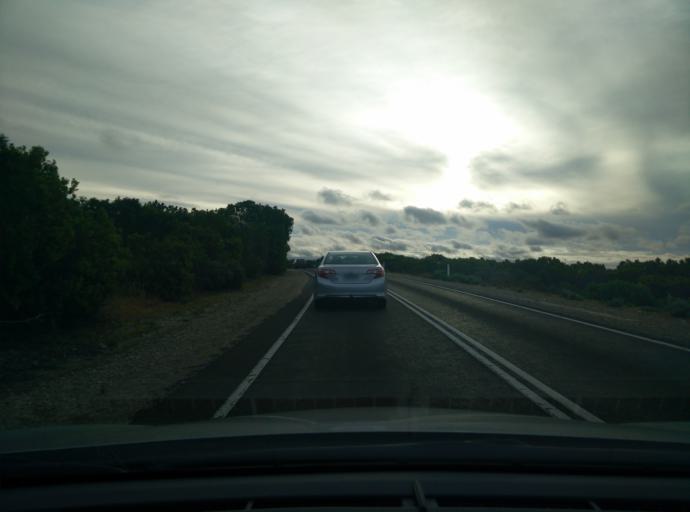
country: AU
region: South Australia
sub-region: Kangaroo Island
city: Kingscote
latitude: -35.8277
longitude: 137.8068
